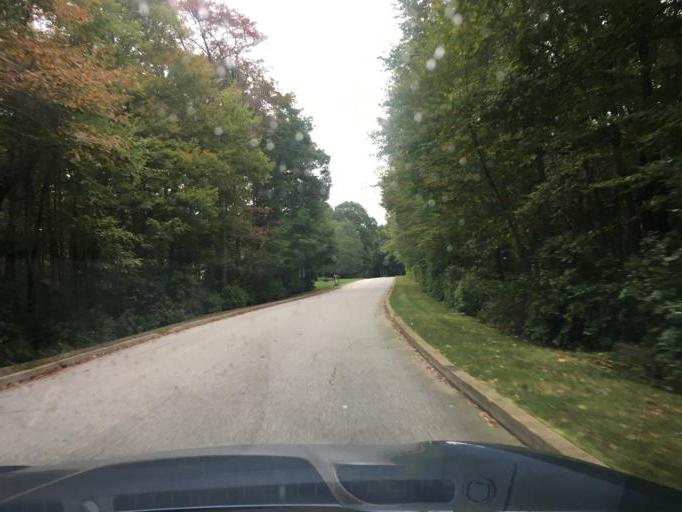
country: US
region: Rhode Island
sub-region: Washington County
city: Exeter
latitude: 41.6126
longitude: -71.5389
